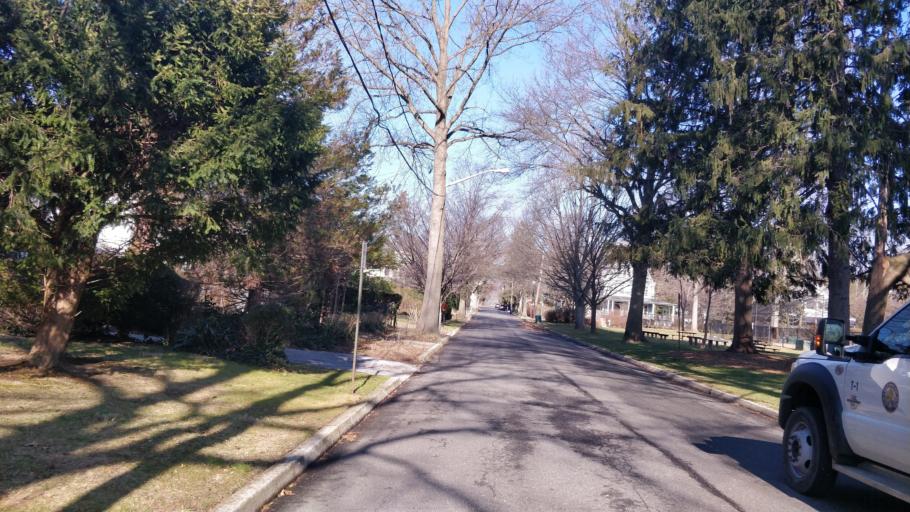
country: US
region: New York
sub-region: Nassau County
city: Sea Cliff
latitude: 40.8487
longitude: -73.6398
